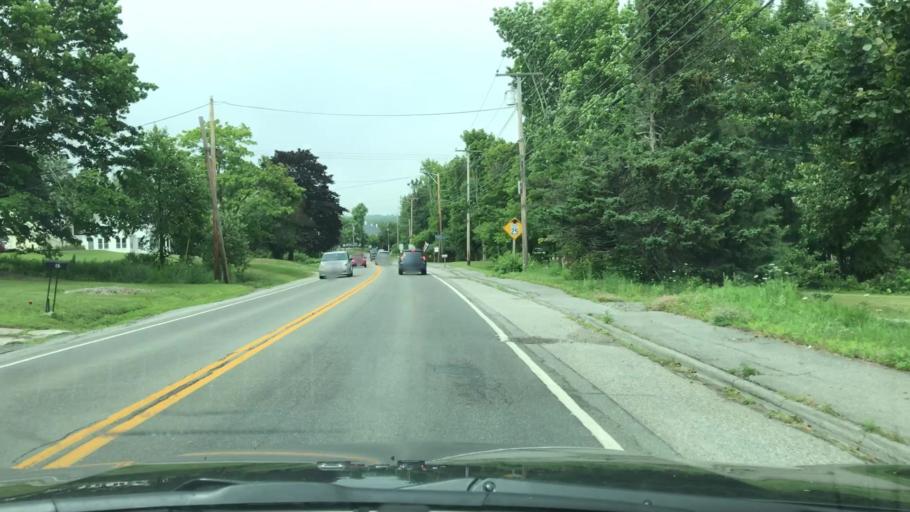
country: US
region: Maine
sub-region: Waldo County
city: Belfast
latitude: 44.4527
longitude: -68.9321
